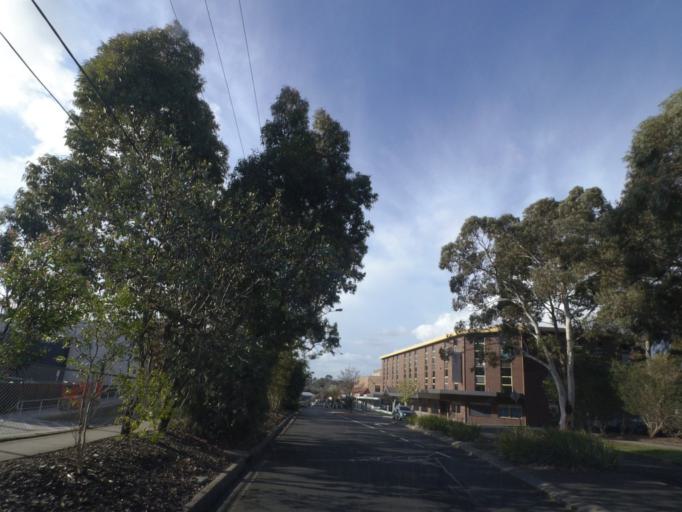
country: AU
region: Victoria
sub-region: Whitehorse
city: Forest Hill
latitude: -37.8369
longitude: 145.1660
